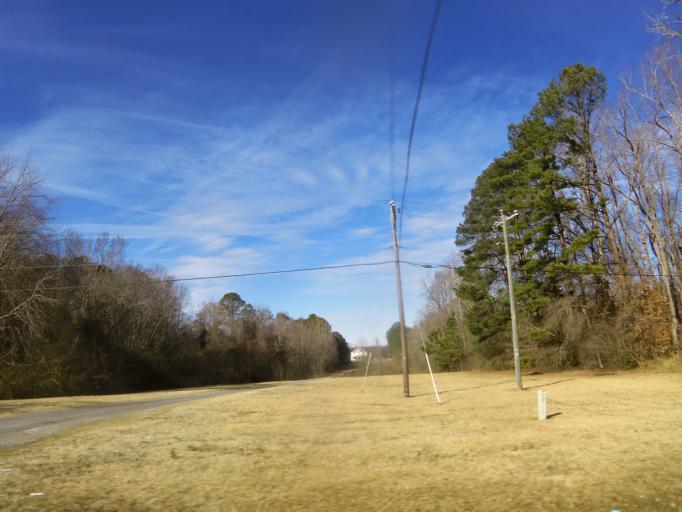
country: US
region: Virginia
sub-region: Isle of Wight County
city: Windsor
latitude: 36.7852
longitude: -76.7958
